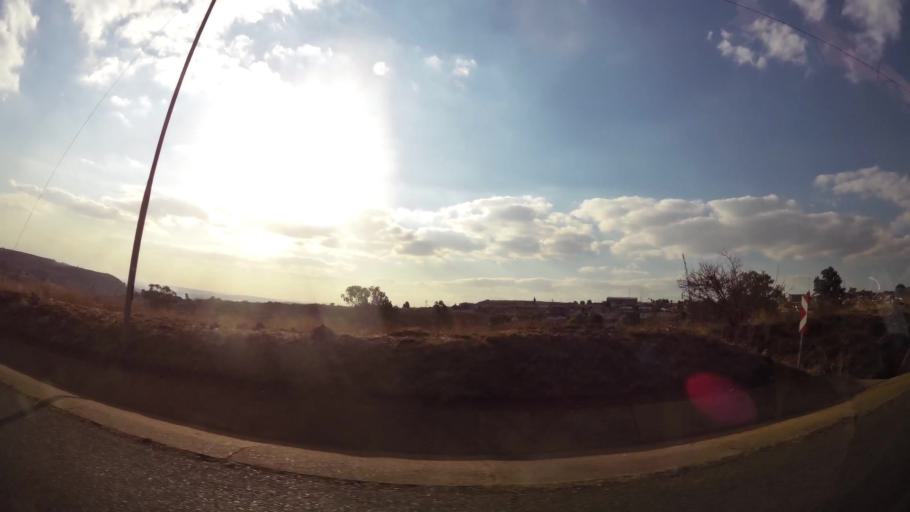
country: ZA
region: Gauteng
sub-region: West Rand District Municipality
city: Krugersdorp
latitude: -26.0846
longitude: 27.7521
